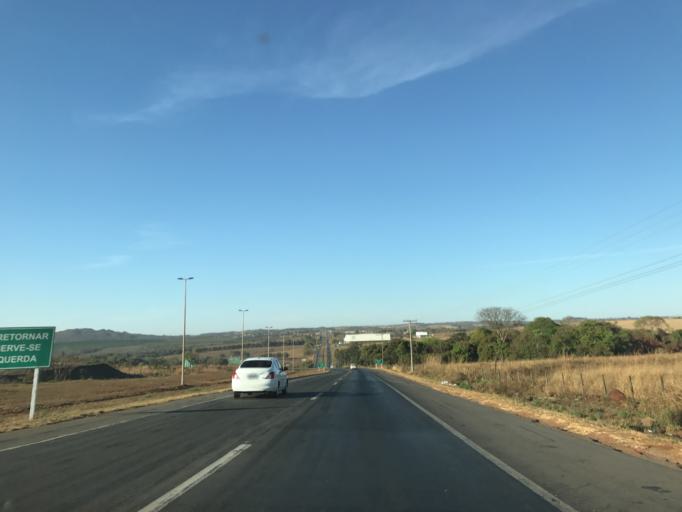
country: BR
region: Goias
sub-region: Aparecida De Goiania
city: Aparecida de Goiania
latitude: -16.8420
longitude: -49.2455
